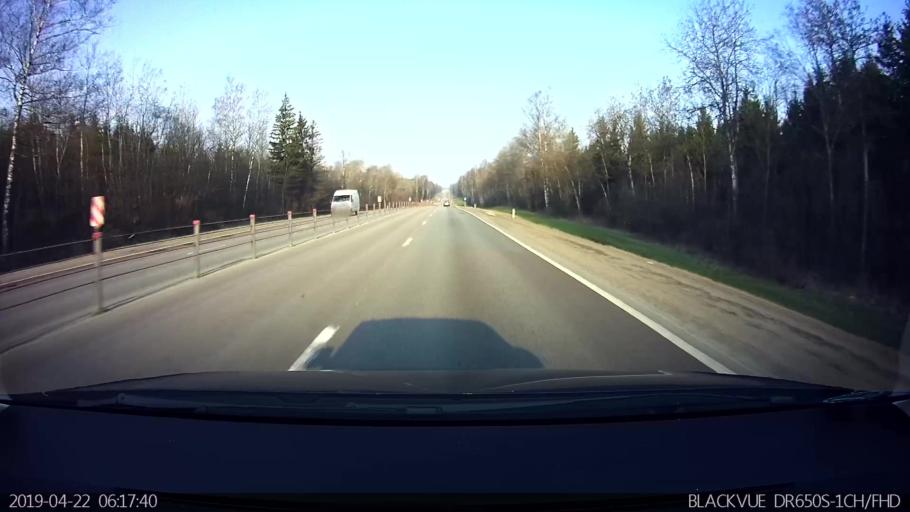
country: RU
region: Moskovskaya
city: Mozhaysk
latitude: 55.4620
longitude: 35.9837
